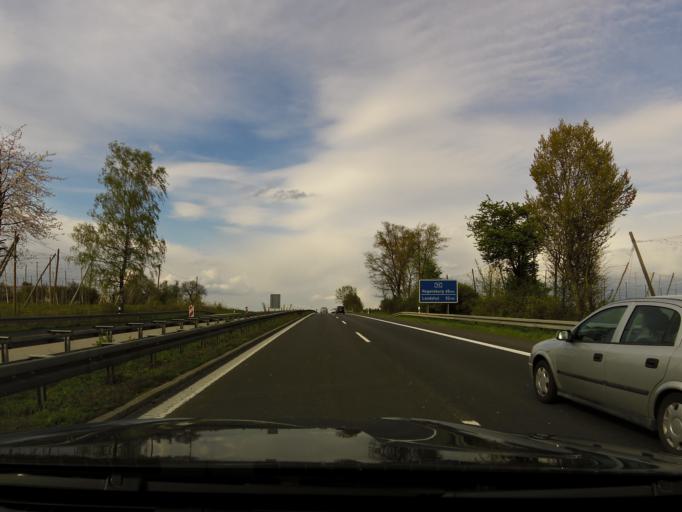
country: DE
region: Bavaria
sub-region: Upper Bavaria
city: Wolnzach
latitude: 48.5852
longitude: 11.6001
